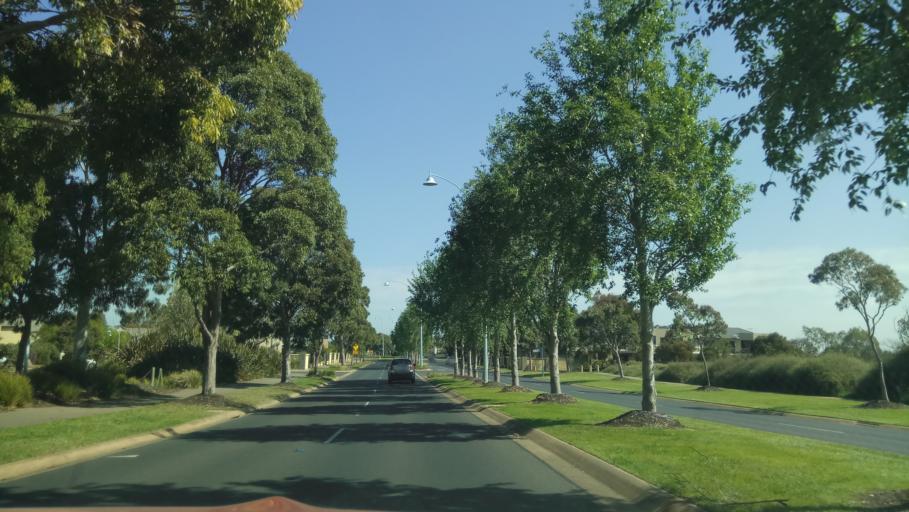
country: AU
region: Victoria
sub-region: Hobsons Bay
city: Altona Meadows
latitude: -37.8915
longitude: 144.7615
